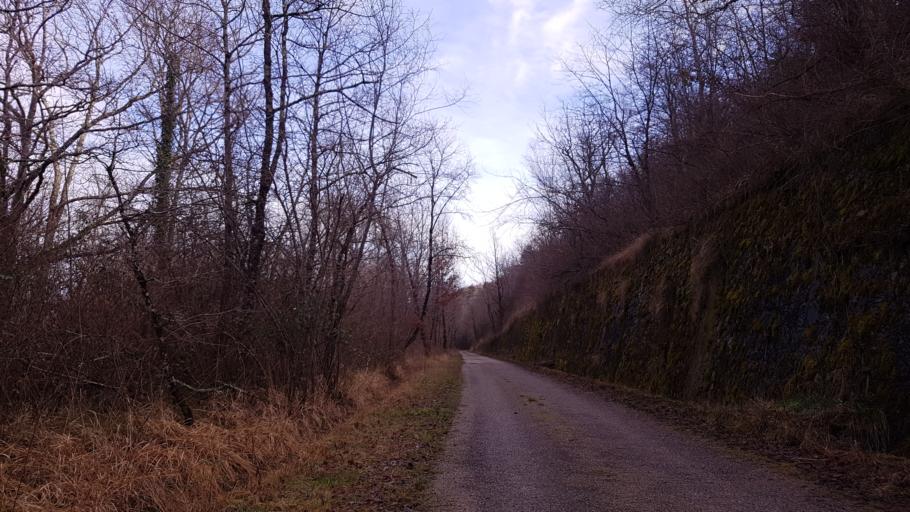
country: FR
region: Languedoc-Roussillon
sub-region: Departement de l'Aude
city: Chalabre
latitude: 43.0080
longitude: 1.9673
